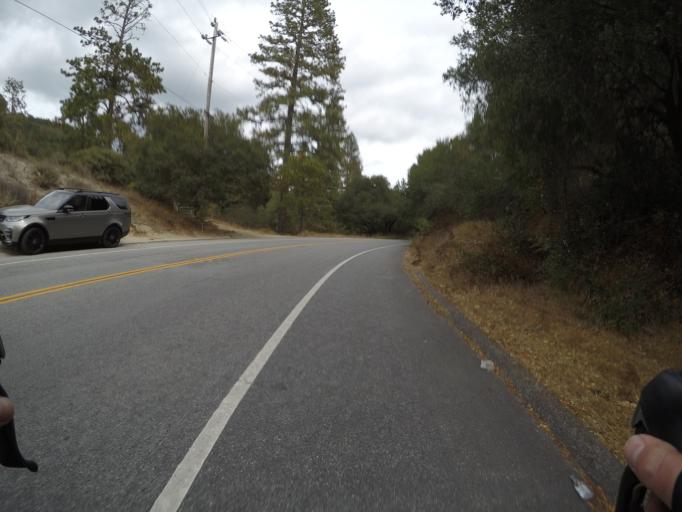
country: US
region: California
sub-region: Santa Cruz County
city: Ben Lomond
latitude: 37.0859
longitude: -122.0671
